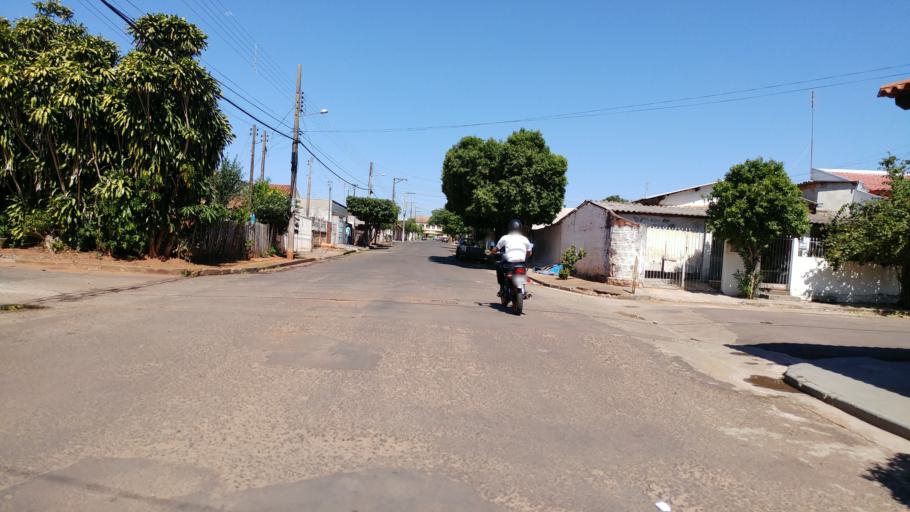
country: BR
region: Sao Paulo
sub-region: Paraguacu Paulista
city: Paraguacu Paulista
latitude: -22.4227
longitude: -50.5846
